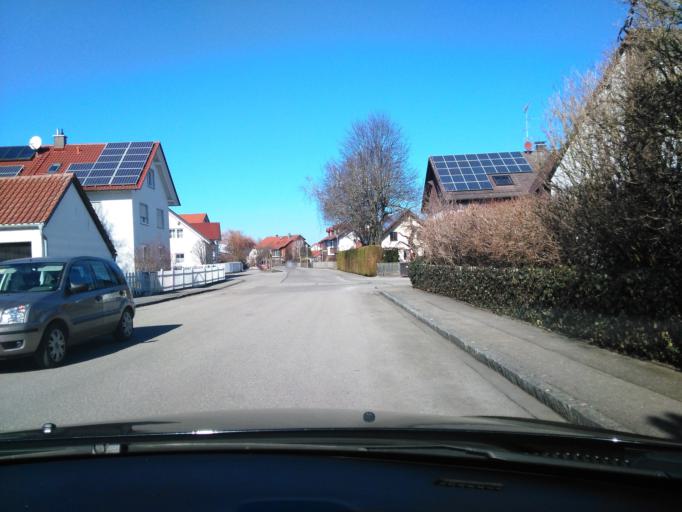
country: DE
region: Bavaria
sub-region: Upper Bavaria
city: Mammendorf
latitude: 48.2103
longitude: 11.1718
